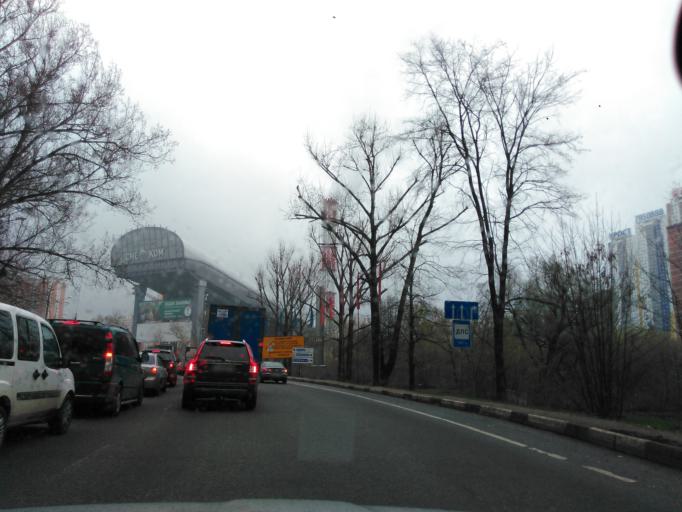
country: RU
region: Moskovskaya
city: Pavshino
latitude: 55.8174
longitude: 37.3539
